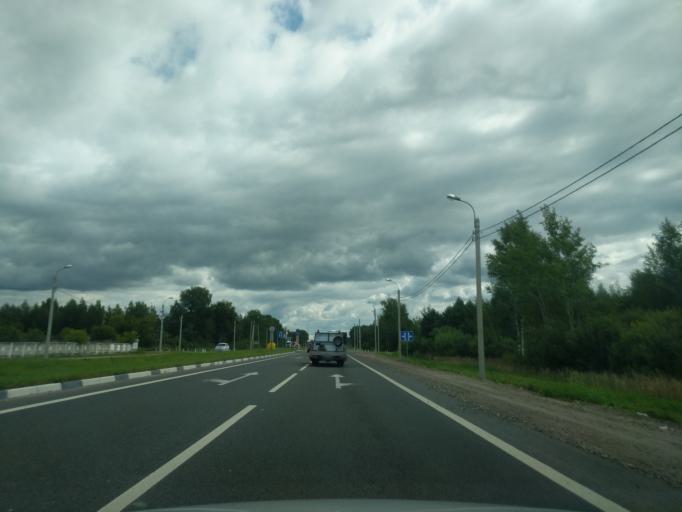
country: RU
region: Jaroslavl
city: Tunoshna
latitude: 57.5406
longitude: 39.9873
